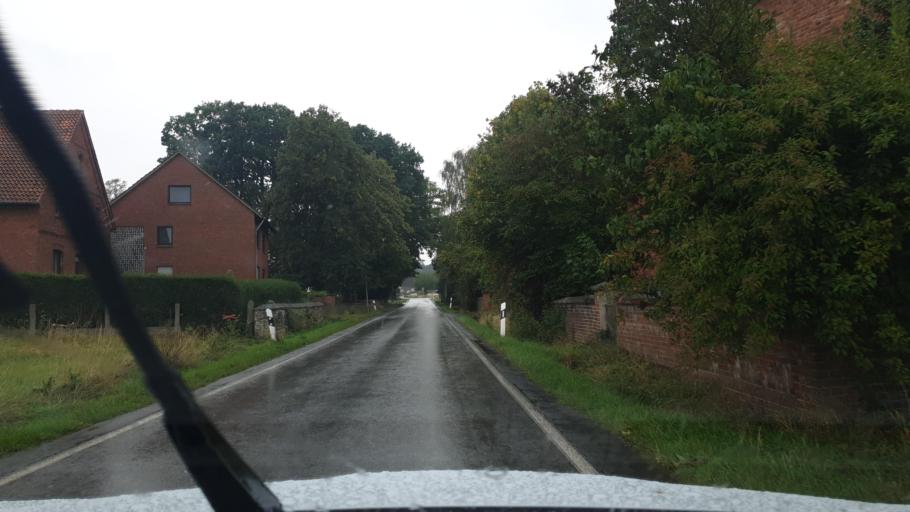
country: DE
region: North Rhine-Westphalia
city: Porta Westfalica
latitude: 52.2030
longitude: 8.8965
